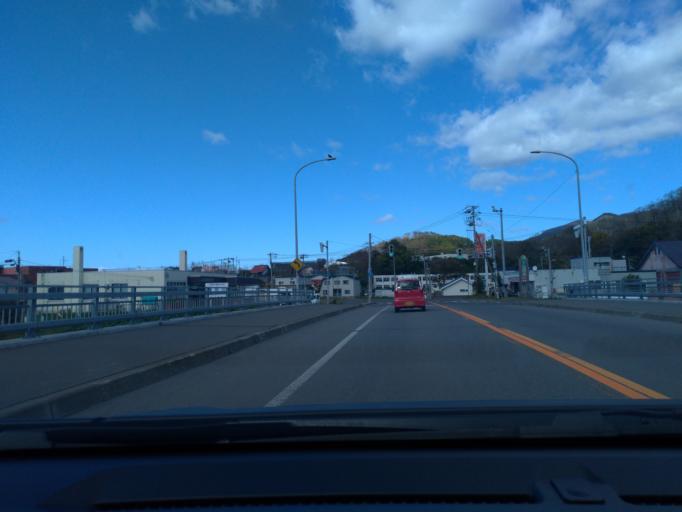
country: JP
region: Hokkaido
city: Ishikari
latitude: 43.3986
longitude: 141.4364
